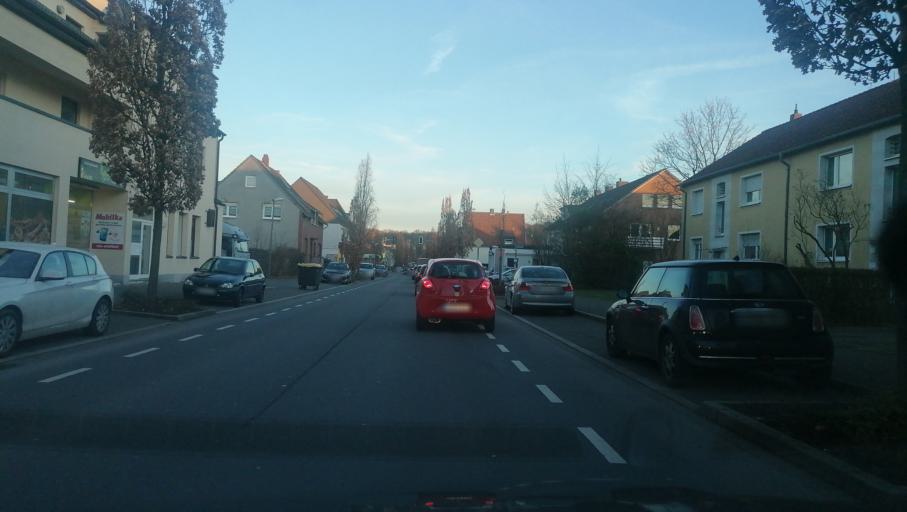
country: DE
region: North Rhine-Westphalia
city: Bergkamen
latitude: 51.6067
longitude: 7.6188
